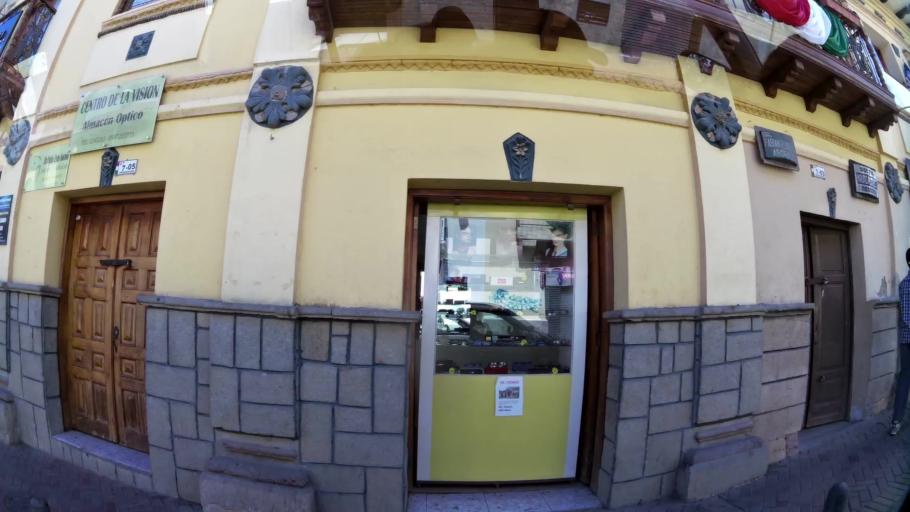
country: EC
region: Canar
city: Azogues
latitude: -2.7398
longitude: -78.8461
